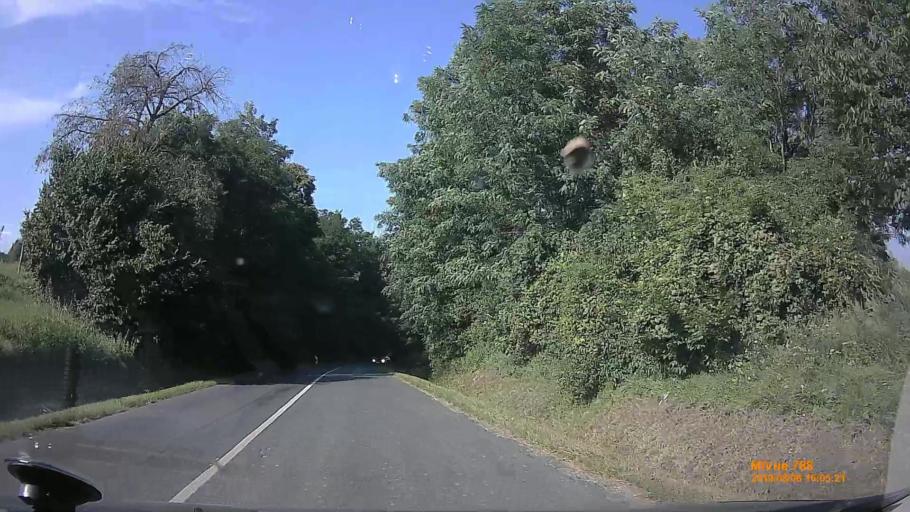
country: HU
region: Zala
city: Murakeresztur
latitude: 46.3118
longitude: 16.9621
